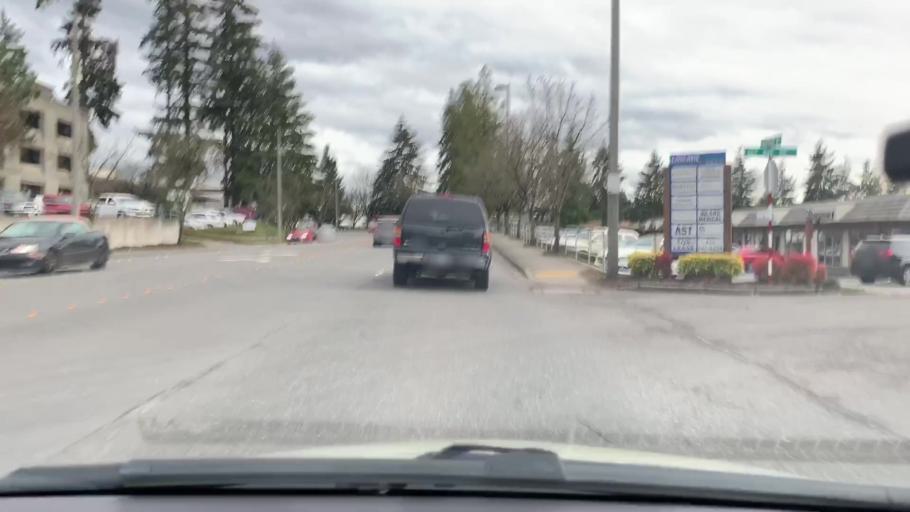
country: US
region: Washington
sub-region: King County
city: Bellevue
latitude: 47.6284
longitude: -122.1710
